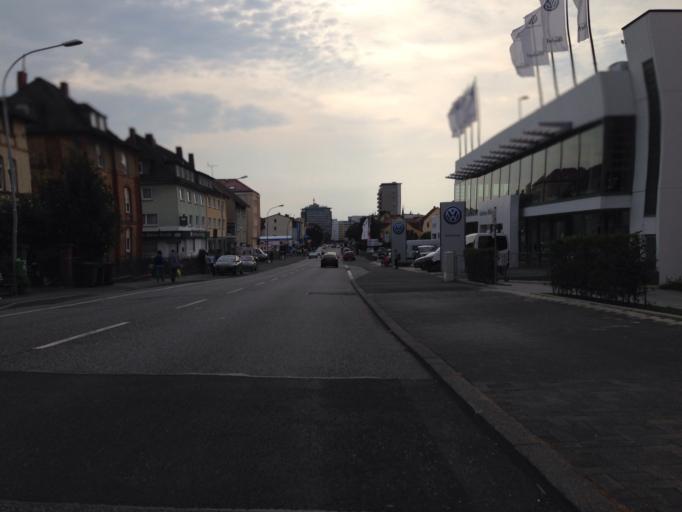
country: DE
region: Hesse
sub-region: Regierungsbezirk Giessen
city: Giessen
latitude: 50.5848
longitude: 8.6902
